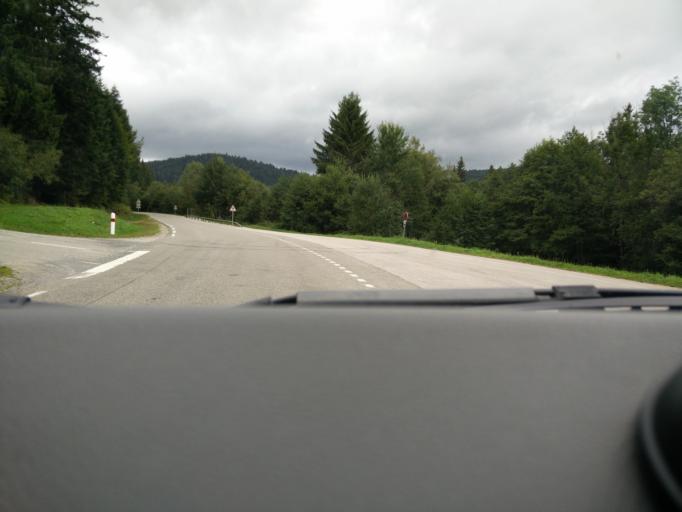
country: FR
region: Lorraine
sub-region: Departement des Vosges
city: Xonrupt-Longemer
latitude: 48.0781
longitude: 6.9409
